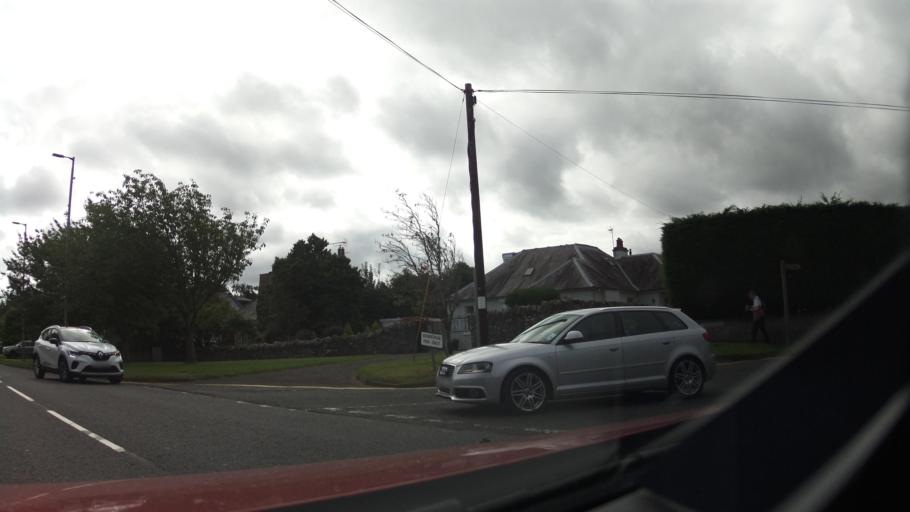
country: GB
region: Scotland
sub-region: The Scottish Borders
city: Lauder
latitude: 55.7235
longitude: -2.7570
